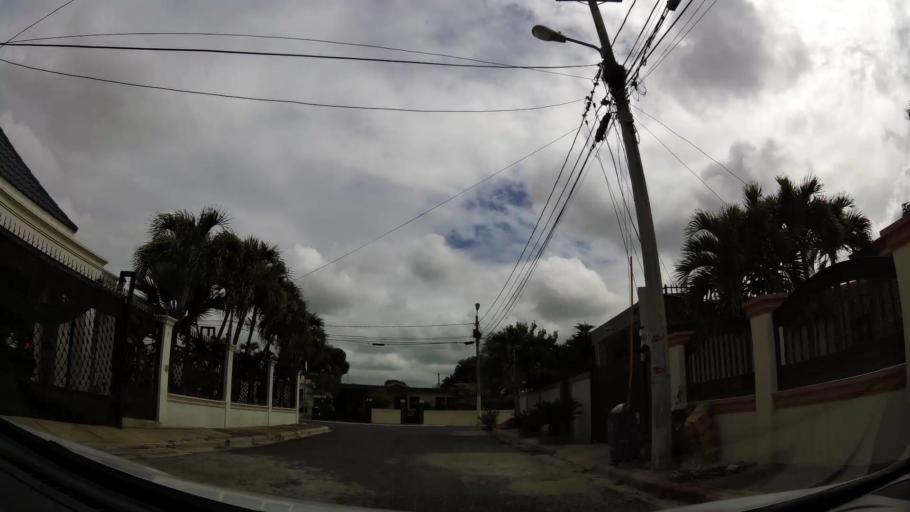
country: DO
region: Santiago
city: Santiago de los Caballeros
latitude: 19.4407
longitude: -70.6728
